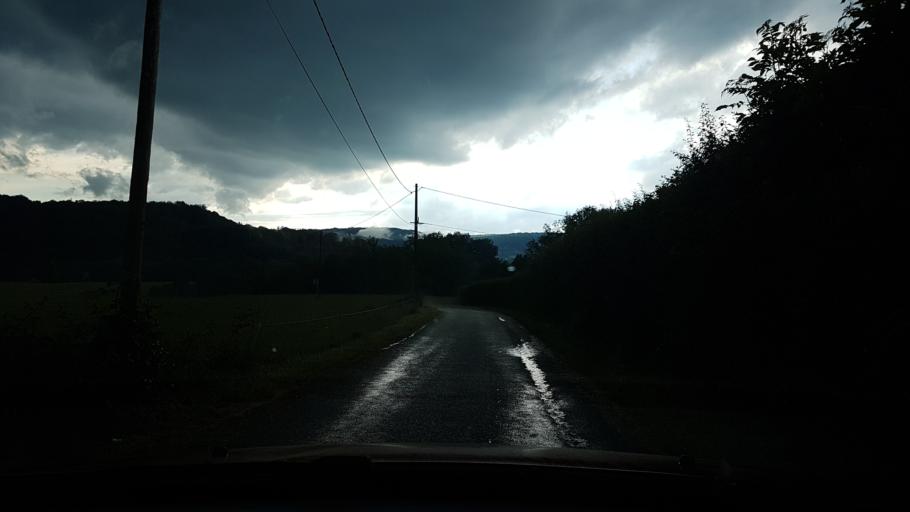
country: FR
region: Franche-Comte
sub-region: Departement du Jura
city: Clairvaux-les-Lacs
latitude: 46.5488
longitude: 5.7087
